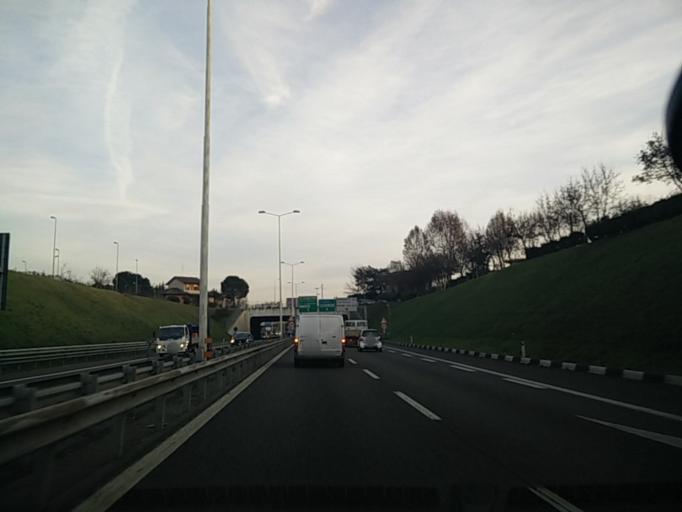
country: IT
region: Lombardy
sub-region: Citta metropolitana di Milano
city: Cinisello Balsamo
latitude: 45.5625
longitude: 9.2373
